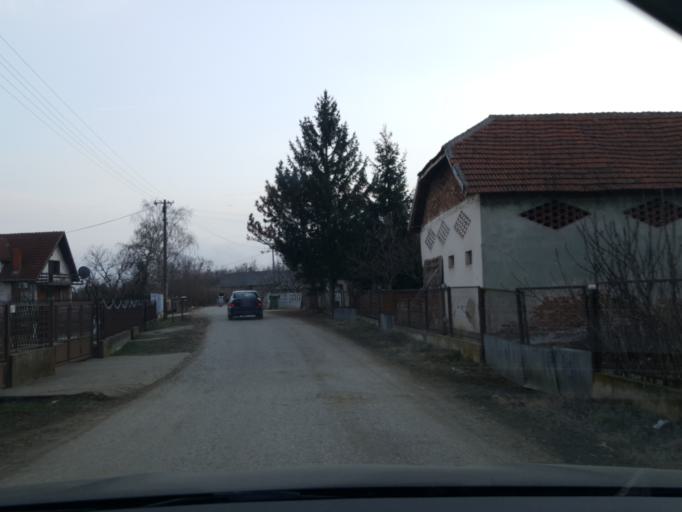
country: RS
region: Central Serbia
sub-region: Nisavski Okrug
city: Aleksinac
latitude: 43.5767
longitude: 21.6465
